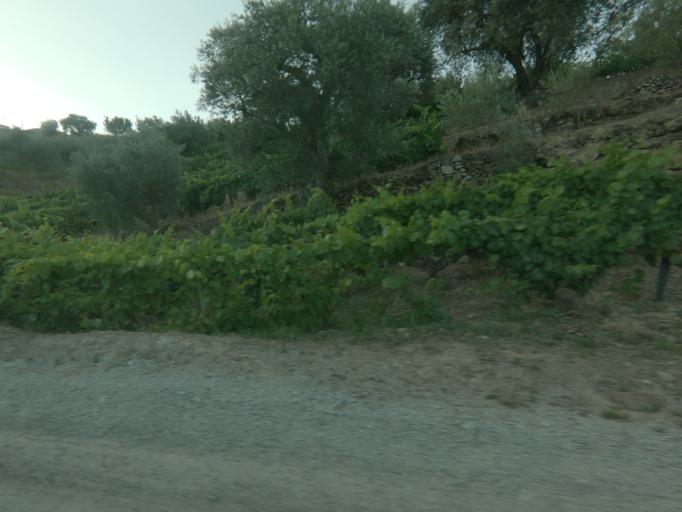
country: PT
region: Viseu
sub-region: Armamar
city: Armamar
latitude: 41.1814
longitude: -7.6895
